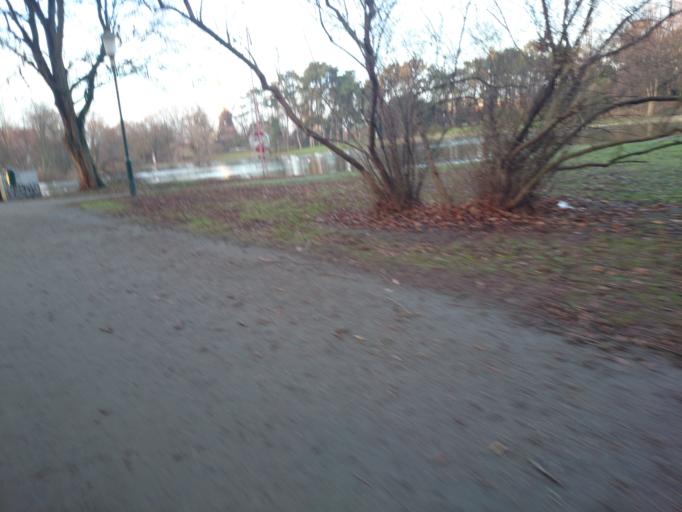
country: SE
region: Skane
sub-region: Malmo
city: Malmoe
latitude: 55.6011
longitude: 12.9880
